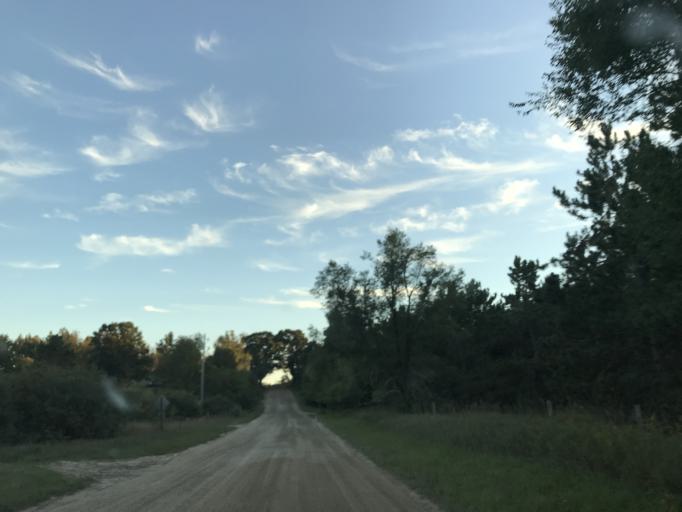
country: US
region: Michigan
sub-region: Mason County
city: Scottville
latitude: 43.9309
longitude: -86.1689
